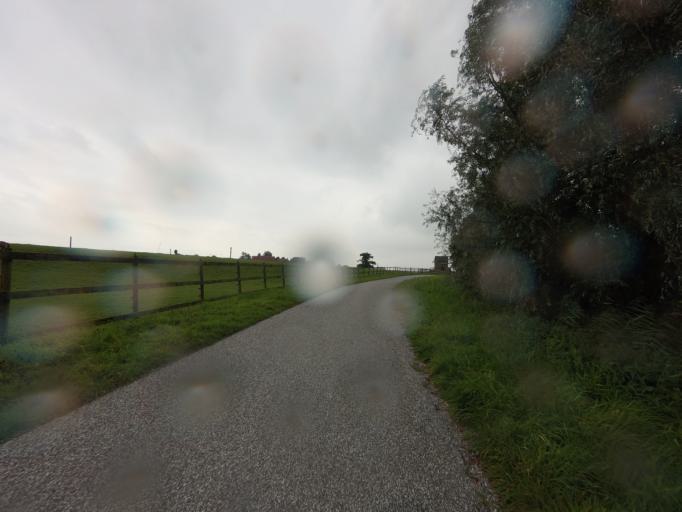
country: NL
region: Friesland
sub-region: Sudwest Fryslan
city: Koudum
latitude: 52.9461
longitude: 5.4355
